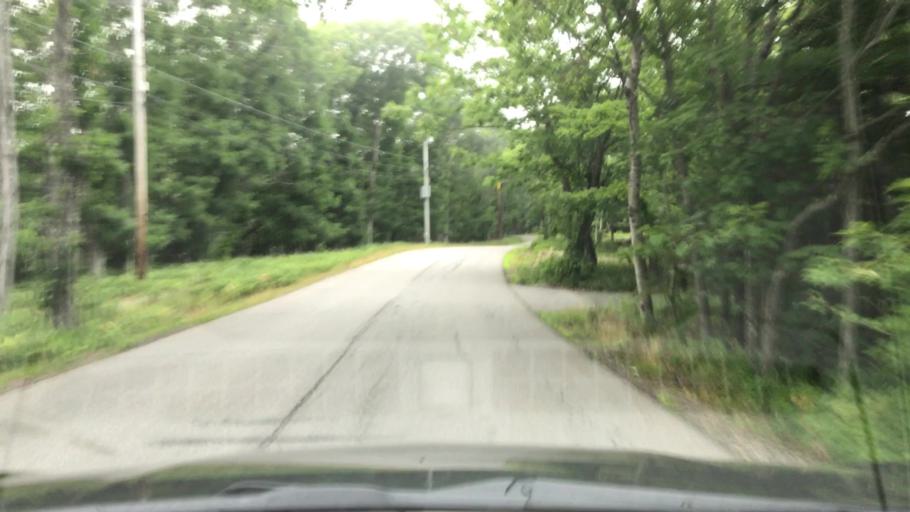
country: US
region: Maine
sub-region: Hancock County
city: Bar Harbor
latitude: 44.3438
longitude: -68.1794
